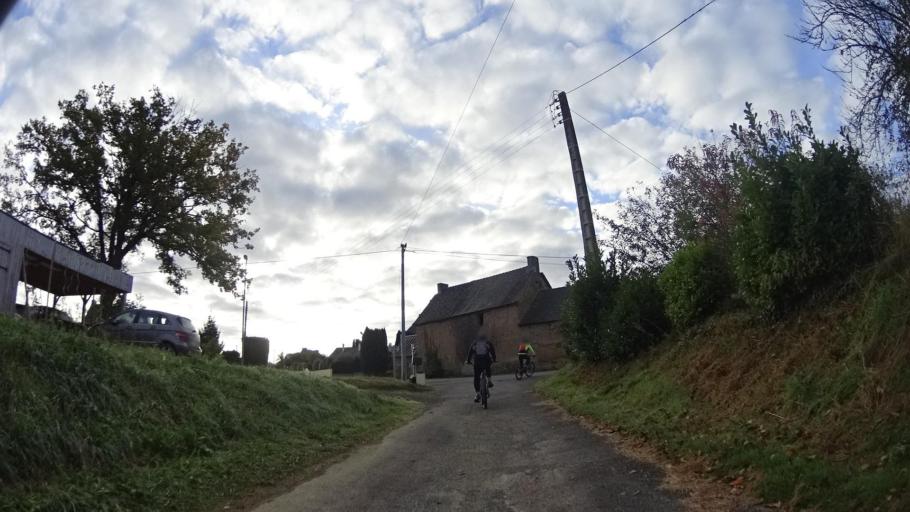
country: FR
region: Brittany
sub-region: Departement des Cotes-d'Armor
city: Evran
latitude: 48.3821
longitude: -1.9682
